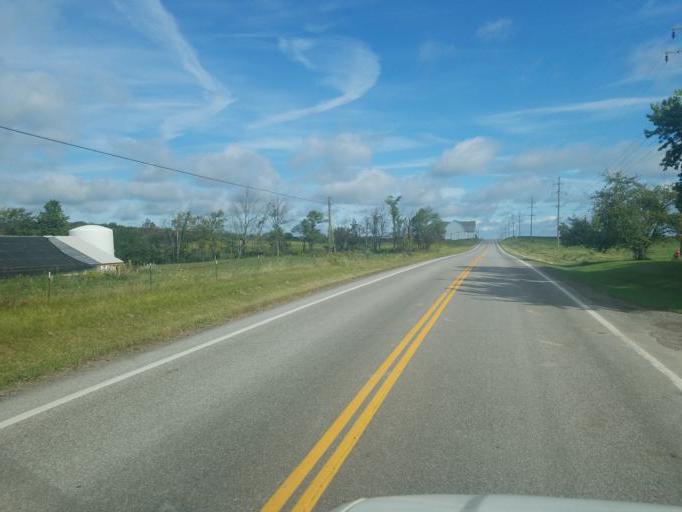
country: US
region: Ohio
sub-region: Wayne County
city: West Salem
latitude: 41.0441
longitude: -82.1259
